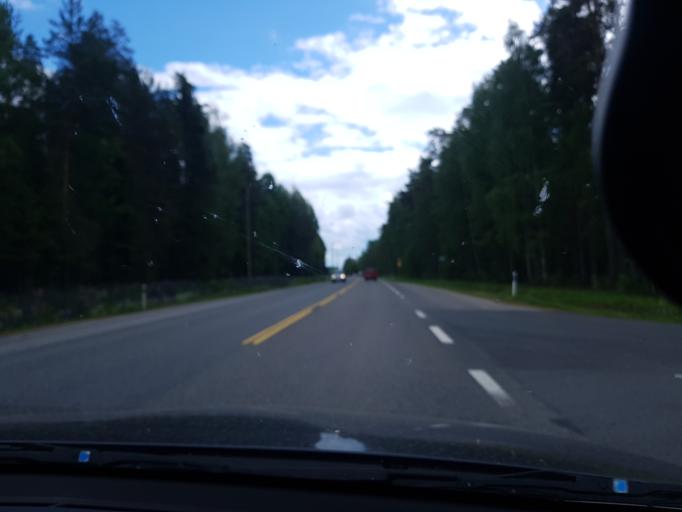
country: FI
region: Pirkanmaa
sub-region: Tampere
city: Paelkaene
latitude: 61.2989
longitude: 24.3060
